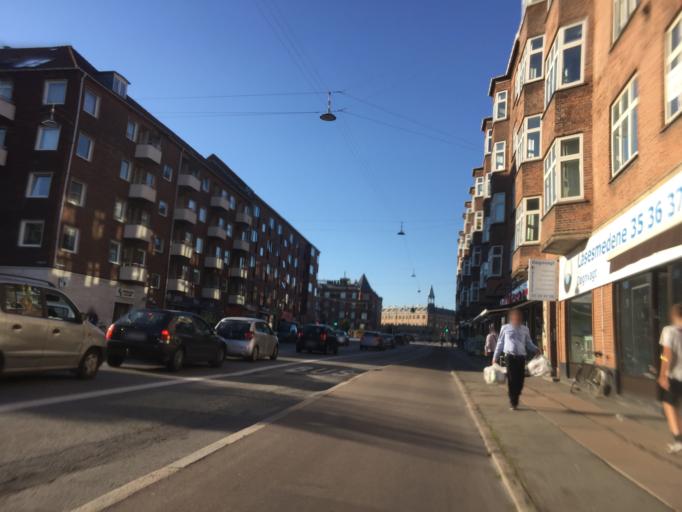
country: DK
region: Capital Region
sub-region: Frederiksberg Kommune
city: Frederiksberg
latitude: 55.6625
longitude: 12.5167
